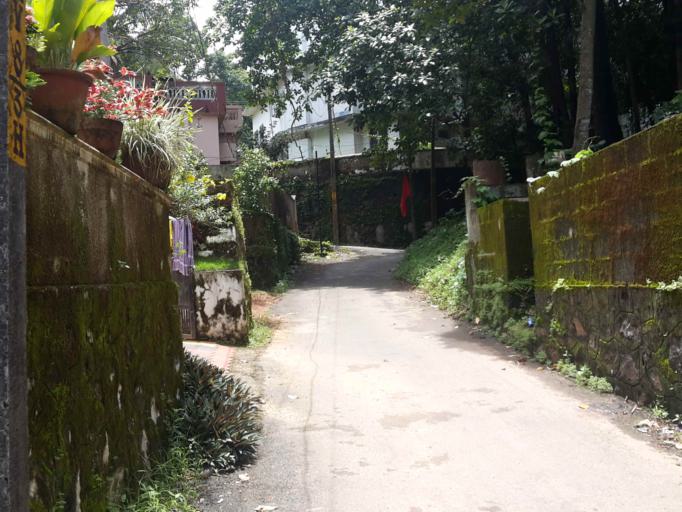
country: IN
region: Kerala
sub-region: Kozhikode
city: Kozhikode
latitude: 11.2860
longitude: 75.7957
